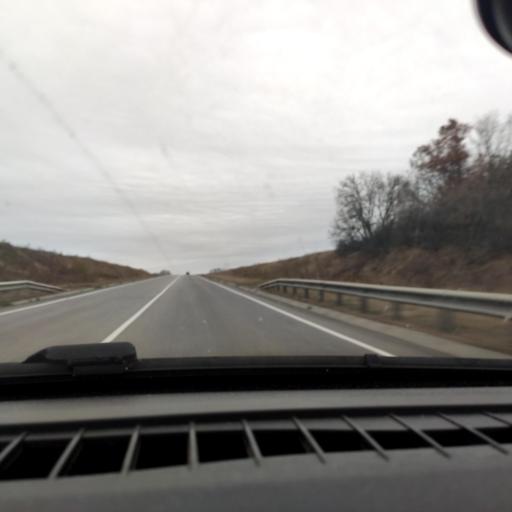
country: RU
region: Voronezj
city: Strelitsa
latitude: 51.5192
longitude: 38.9678
